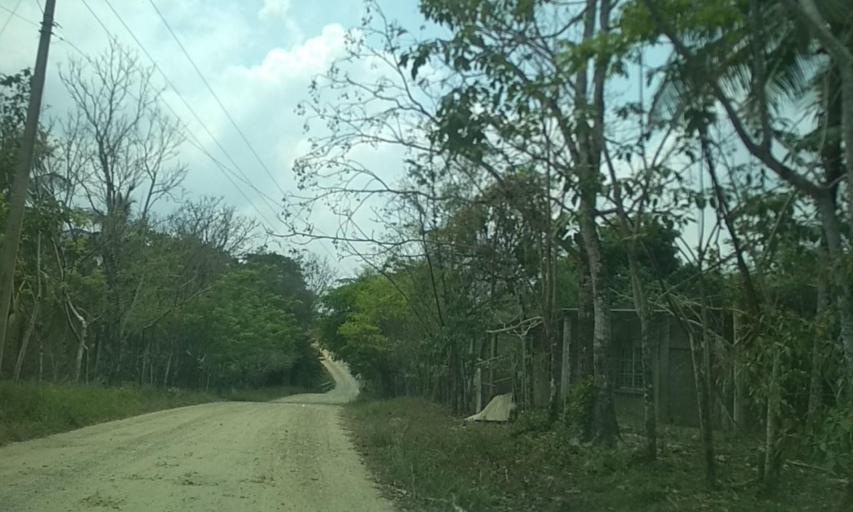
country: MX
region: Tabasco
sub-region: Huimanguillo
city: Francisco Rueda
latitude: 17.6056
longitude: -93.8052
